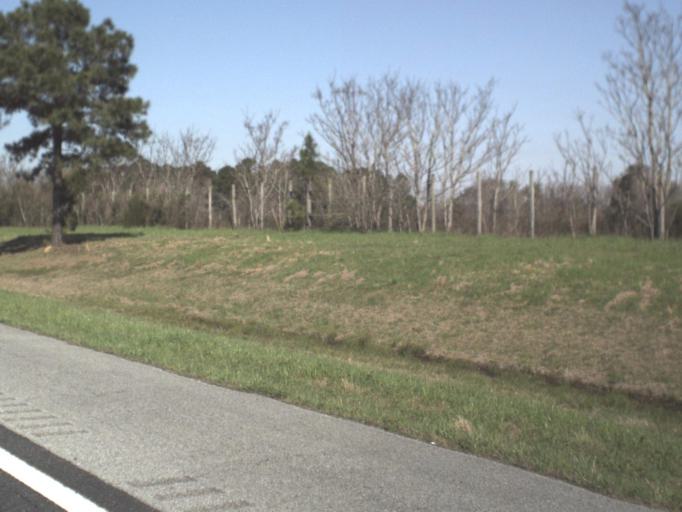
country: US
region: Florida
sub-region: Jackson County
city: Sneads
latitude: 30.6425
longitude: -85.0022
